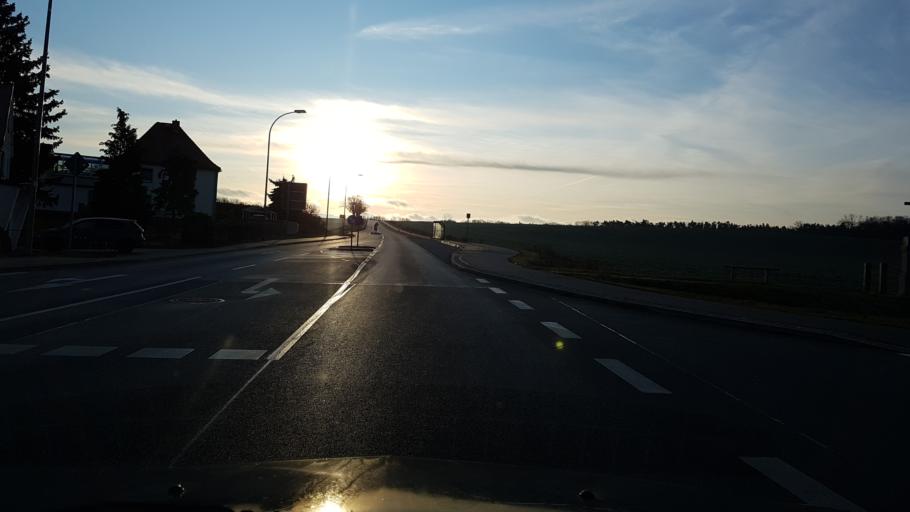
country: DE
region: Saxony
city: Radibor
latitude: 51.2358
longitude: 14.3714
